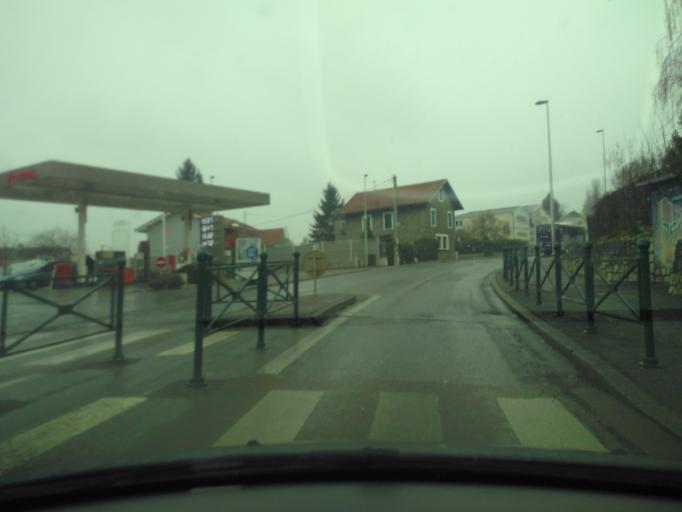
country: FR
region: Rhone-Alpes
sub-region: Departement de la Haute-Savoie
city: Annemasse
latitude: 46.1855
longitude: 6.2305
